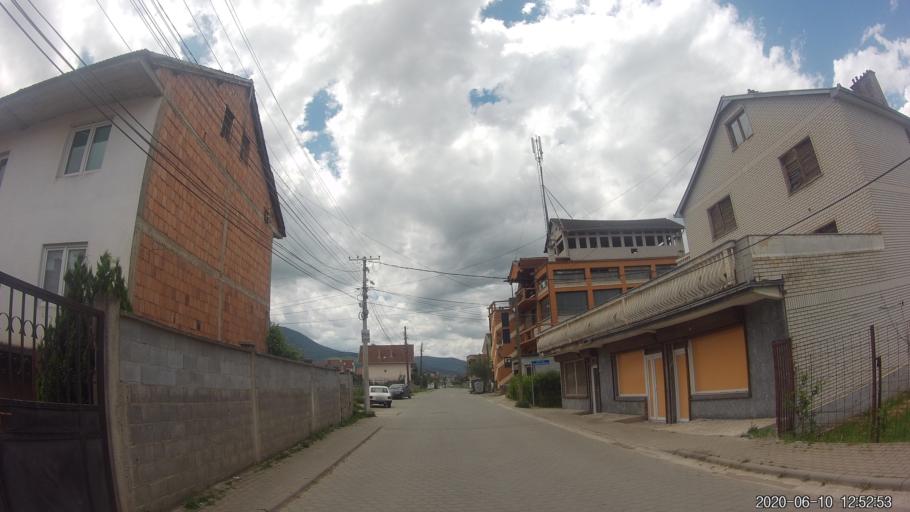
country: XK
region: Prizren
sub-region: Prizren
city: Prizren
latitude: 42.2341
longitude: 20.7630
